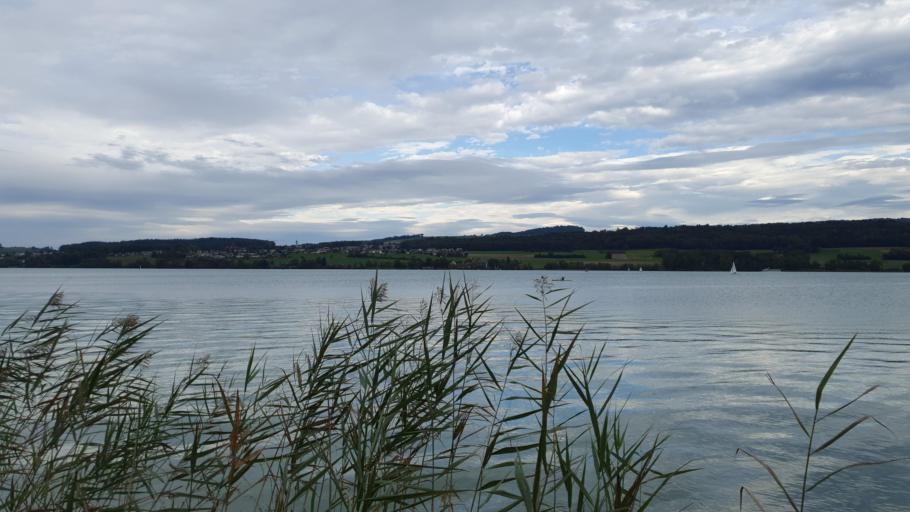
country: CH
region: Aargau
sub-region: Bezirk Kulm
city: Reinach
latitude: 47.2763
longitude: 8.2068
